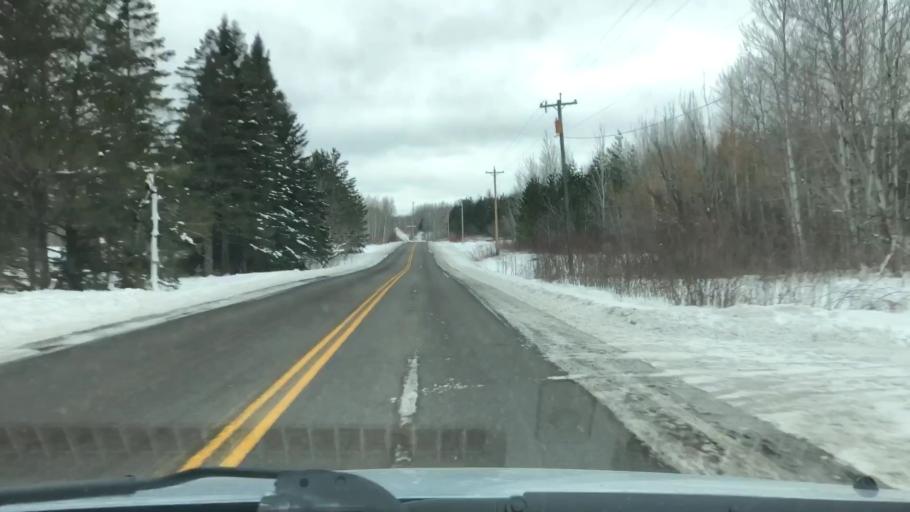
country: US
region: Minnesota
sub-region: Saint Louis County
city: Proctor
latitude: 46.6995
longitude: -92.2809
